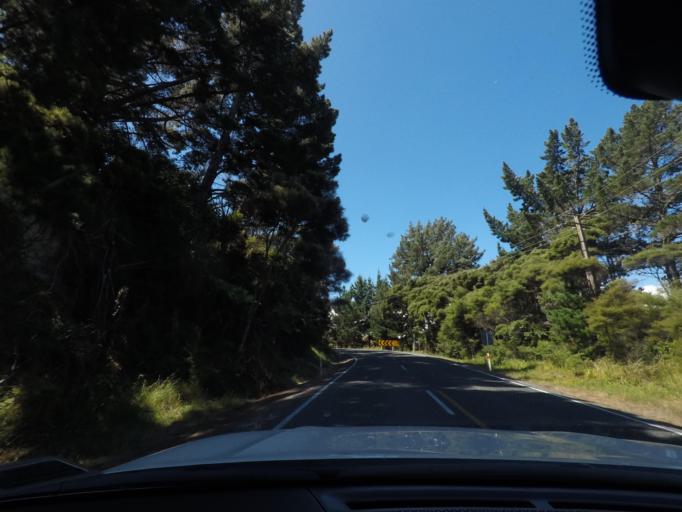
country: NZ
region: Auckland
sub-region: Auckland
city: Parakai
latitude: -36.5997
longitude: 174.3374
